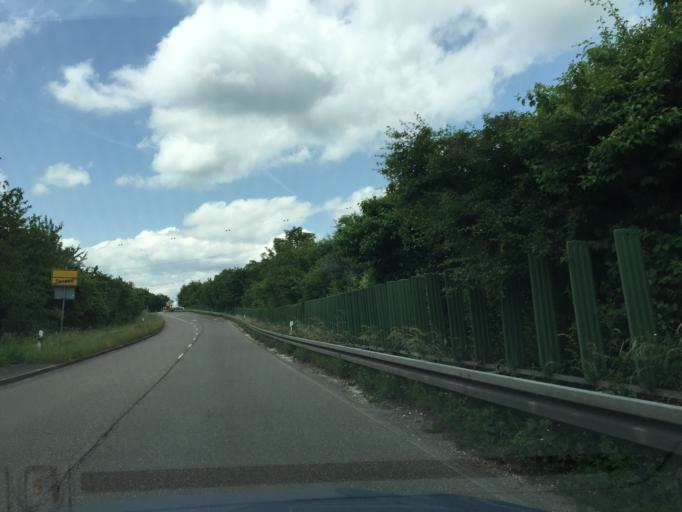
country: DE
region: Bavaria
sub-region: Swabia
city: Senden
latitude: 48.3352
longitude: 10.0376
